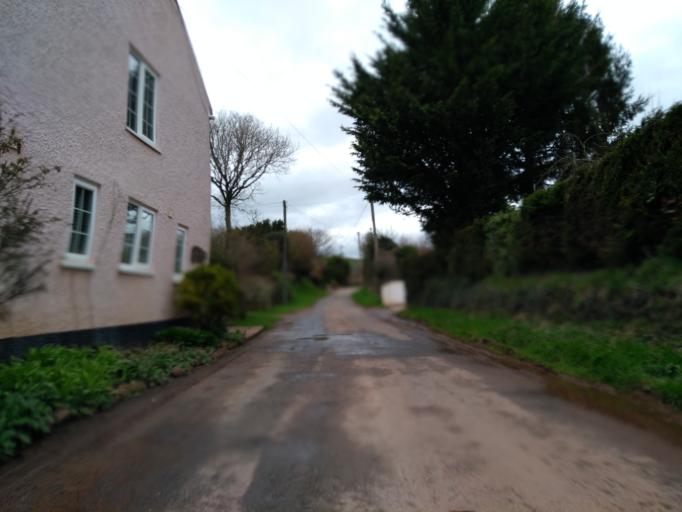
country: GB
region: England
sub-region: Devon
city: Exeter
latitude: 50.8037
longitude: -3.5455
